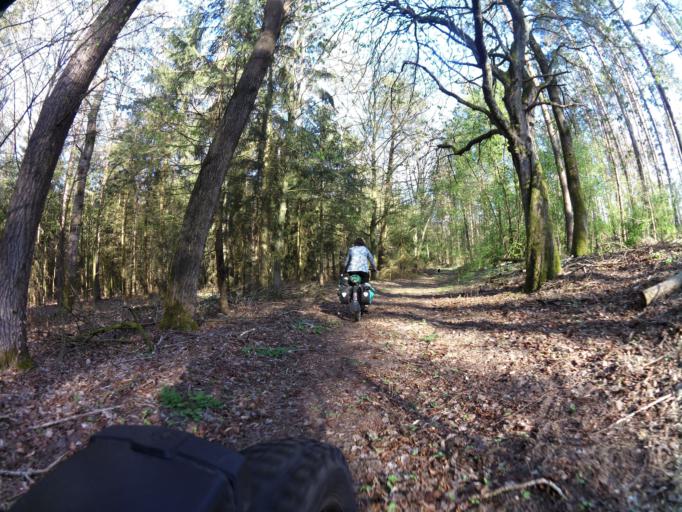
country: PL
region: West Pomeranian Voivodeship
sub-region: Powiat lobeski
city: Lobez
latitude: 53.7515
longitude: 15.6059
